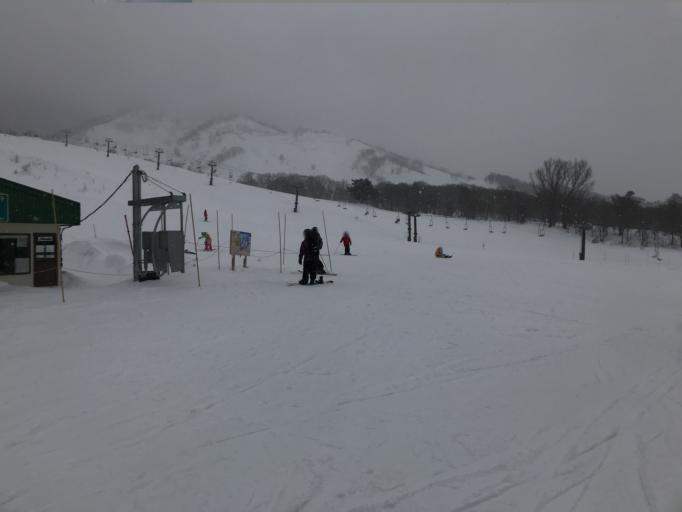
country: JP
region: Nagano
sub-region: Kitaazumi Gun
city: Hakuba
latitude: 36.7564
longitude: 137.8632
